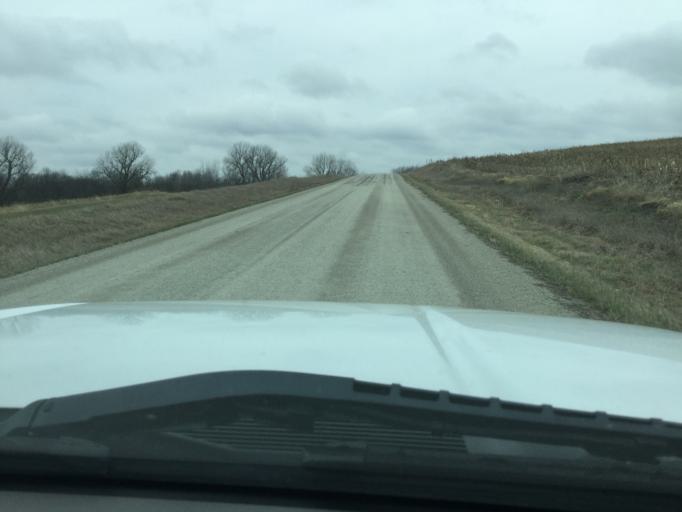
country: US
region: Kansas
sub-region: Nemaha County
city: Sabetha
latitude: 39.7979
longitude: -95.7436
